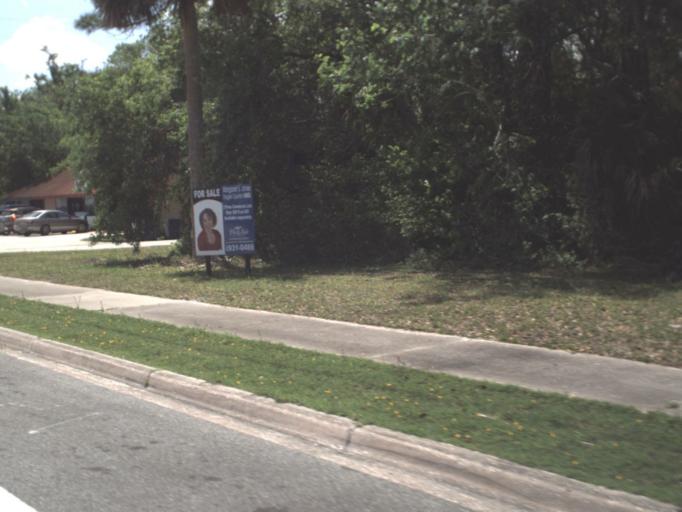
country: US
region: Florida
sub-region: Flagler County
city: Bunnell
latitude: 29.4642
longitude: -81.2555
